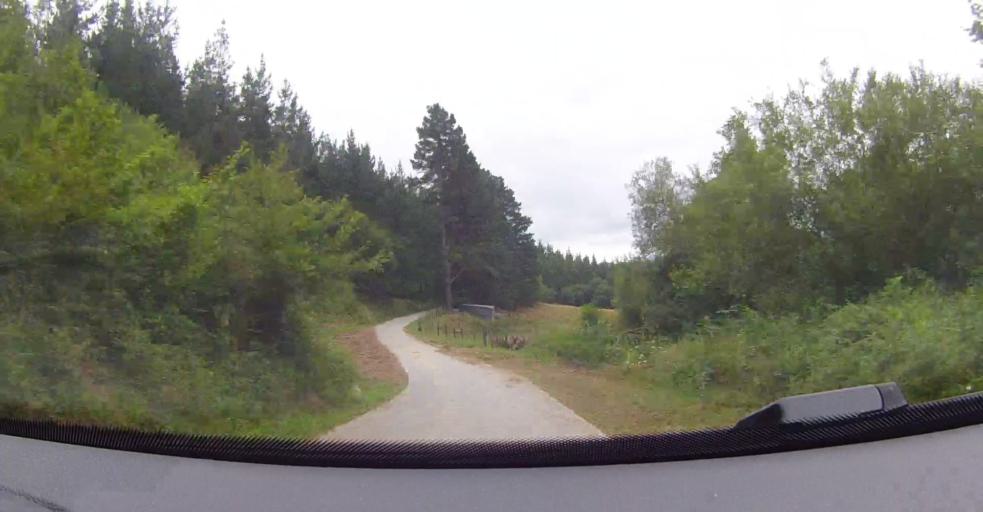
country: ES
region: Basque Country
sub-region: Bizkaia
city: Urrestieta
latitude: 43.2320
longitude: -3.1789
